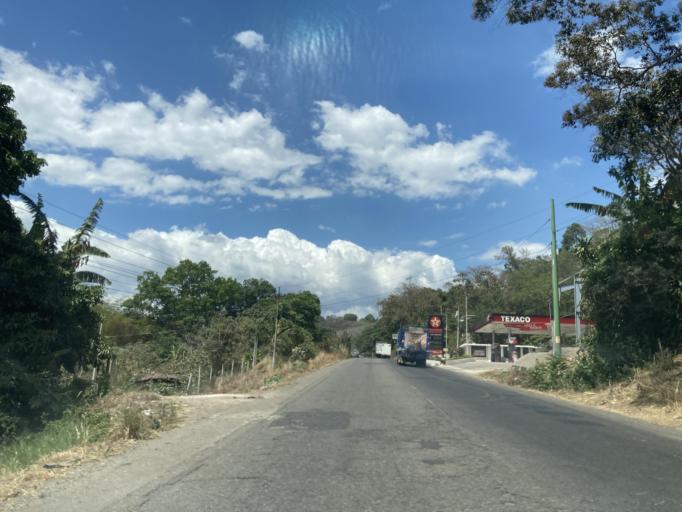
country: GT
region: Santa Rosa
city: Cuilapa
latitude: 14.2749
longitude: -90.3095
